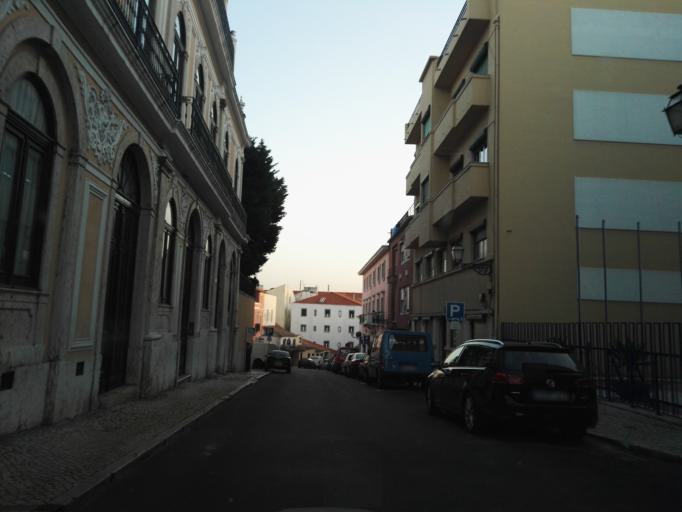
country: PT
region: Lisbon
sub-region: Lisbon
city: Lisbon
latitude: 38.7137
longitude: -9.1514
